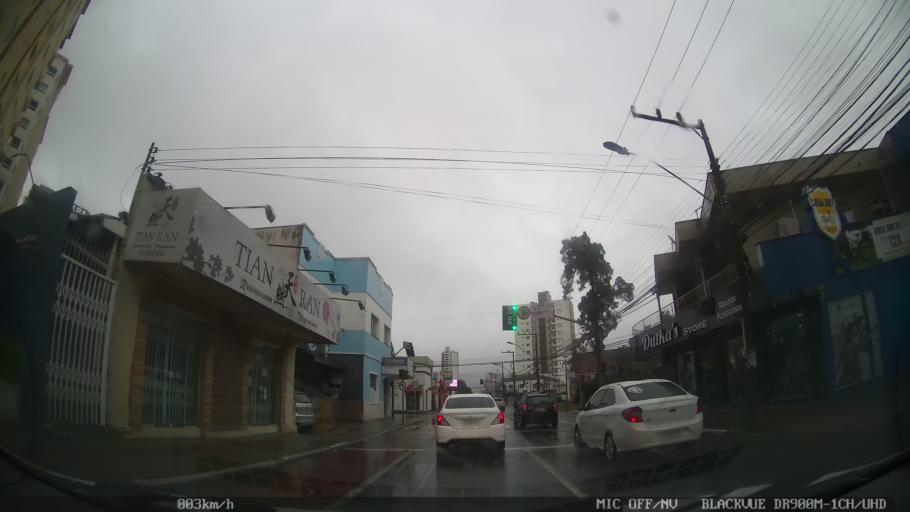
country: BR
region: Santa Catarina
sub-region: Itajai
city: Itajai
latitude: -26.9055
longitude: -48.6687
